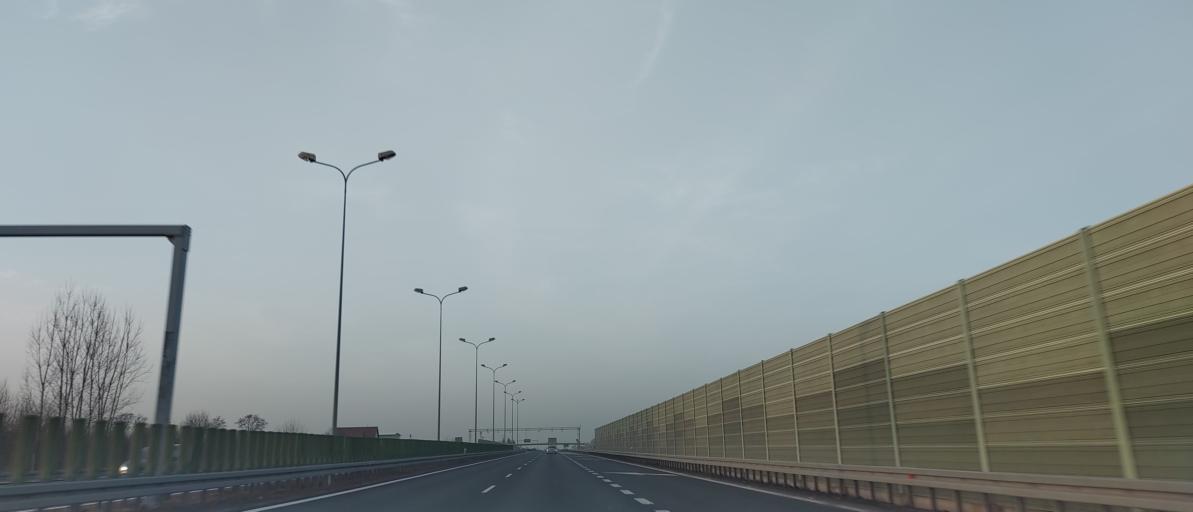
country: PL
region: Masovian Voivodeship
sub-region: Powiat grojecki
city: Goszczyn
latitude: 51.7617
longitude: 20.9032
